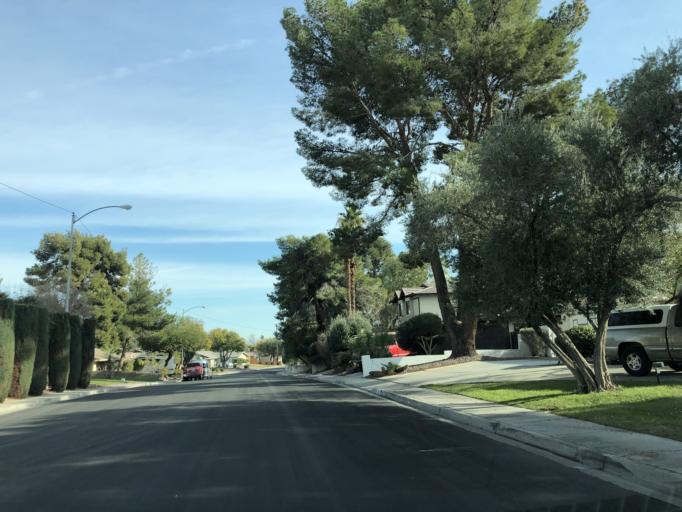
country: US
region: Nevada
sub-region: Clark County
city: Winchester
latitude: 36.1239
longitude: -115.1239
